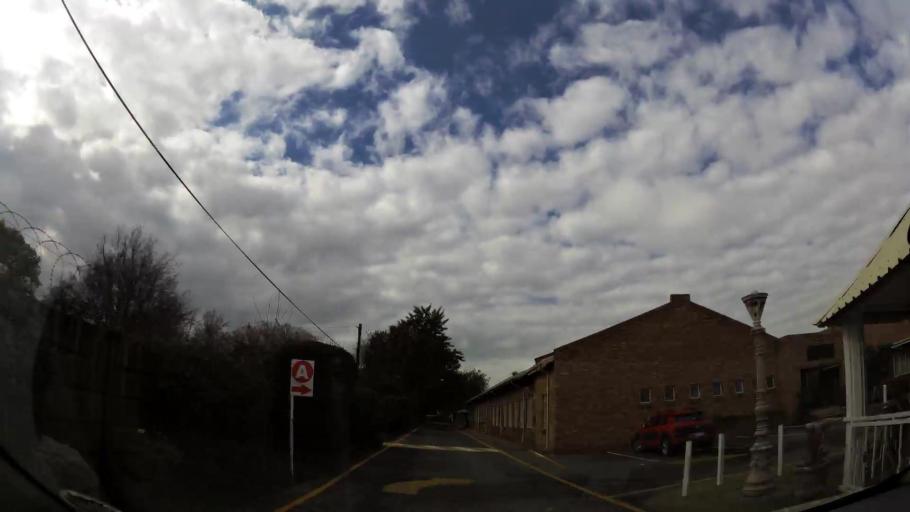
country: ZA
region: Gauteng
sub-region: Sedibeng District Municipality
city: Vereeniging
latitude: -26.6484
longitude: 27.9750
